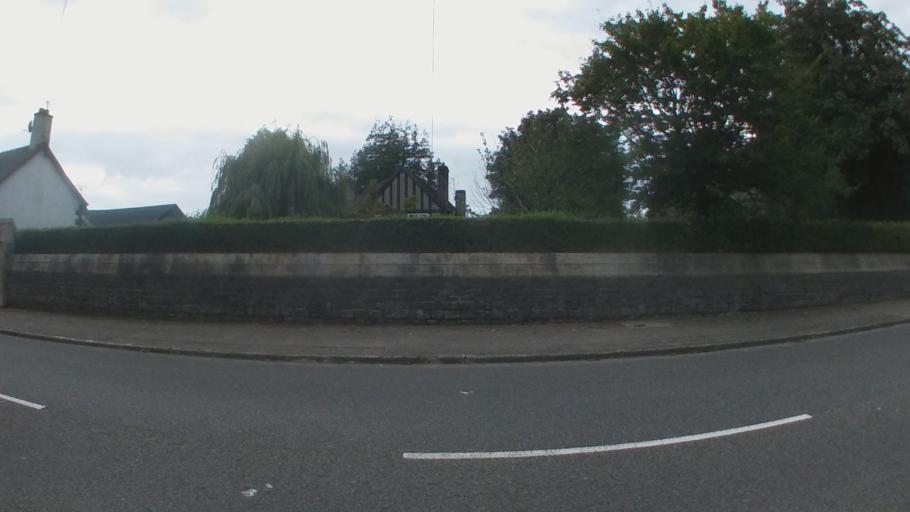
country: IE
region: Leinster
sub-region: County Carlow
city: Carlow
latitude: 52.8426
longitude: -6.9294
